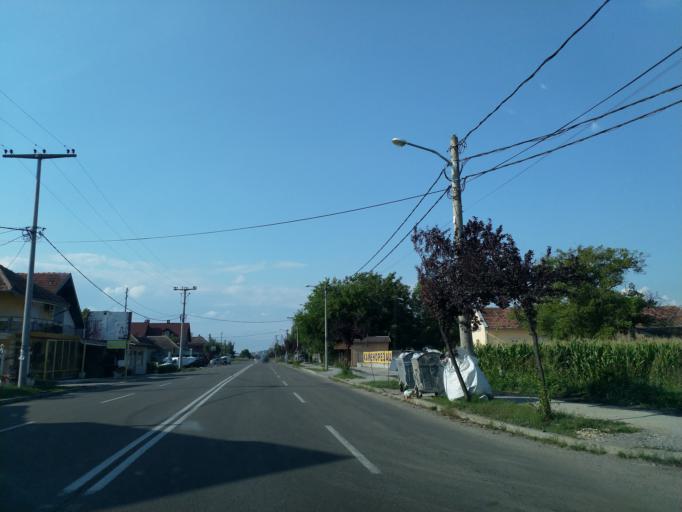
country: RS
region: Central Serbia
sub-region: Pomoravski Okrug
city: Paracin
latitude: 43.8320
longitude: 21.4167
